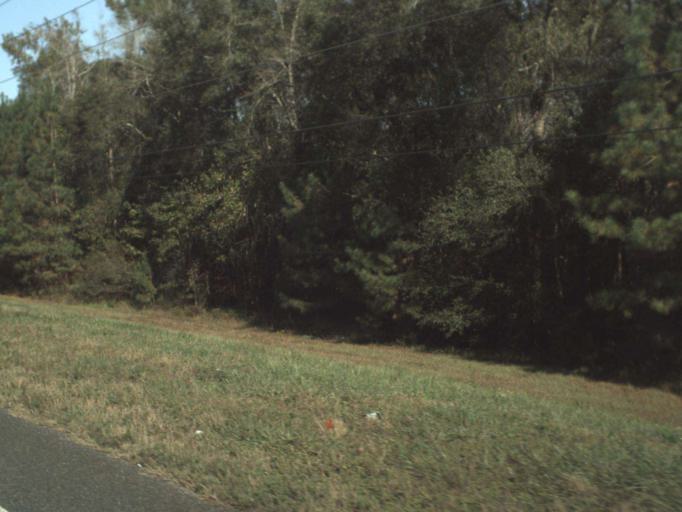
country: US
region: Florida
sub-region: Gadsden County
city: Midway
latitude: 30.4758
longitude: -84.4103
